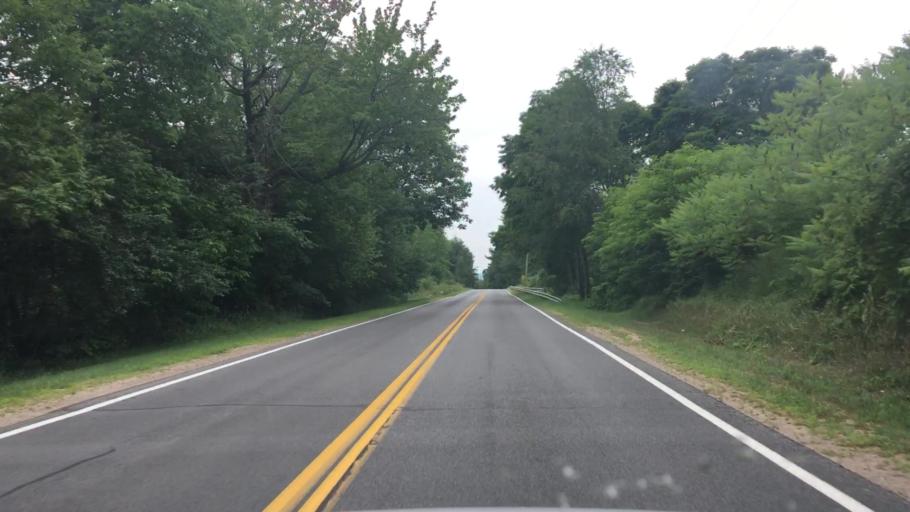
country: US
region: New York
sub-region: Clinton County
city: Morrisonville
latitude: 44.6141
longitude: -73.6366
